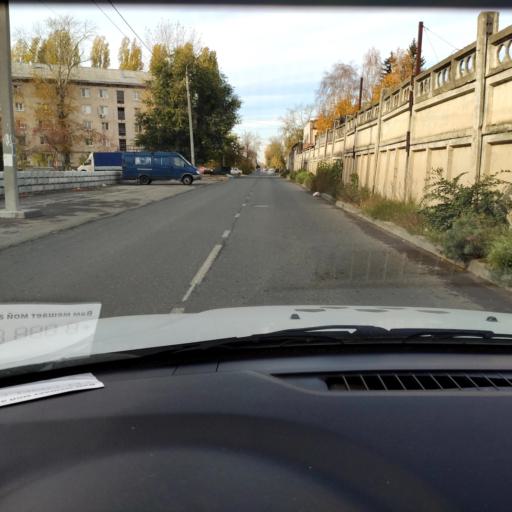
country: RU
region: Samara
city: Tol'yatti
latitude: 53.5249
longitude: 49.4309
